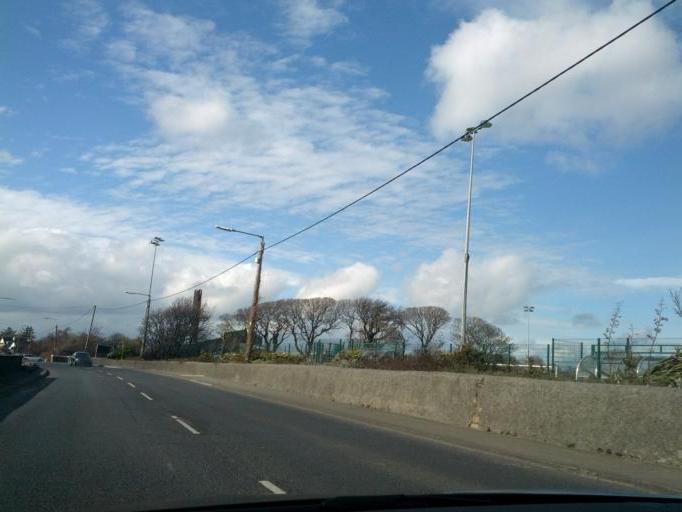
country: IE
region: Leinster
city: Sutton
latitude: 53.3859
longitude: -6.1022
